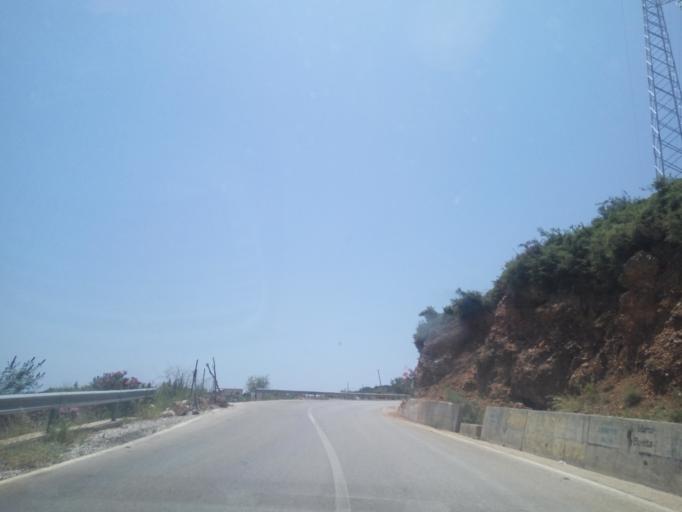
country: AL
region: Vlore
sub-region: Rrethi i Sarandes
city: Lukove
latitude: 40.0596
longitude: 19.8481
